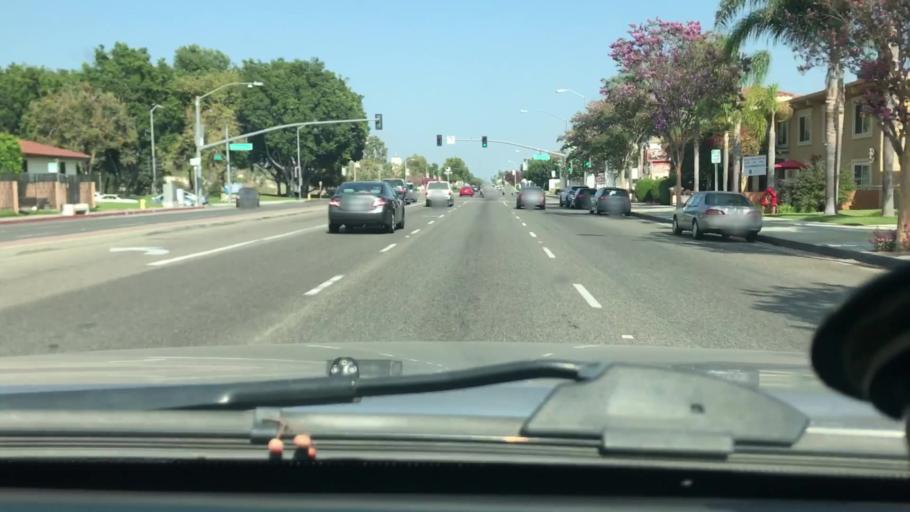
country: US
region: California
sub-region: Orange County
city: Los Alamitos
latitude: 33.8030
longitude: -118.0642
